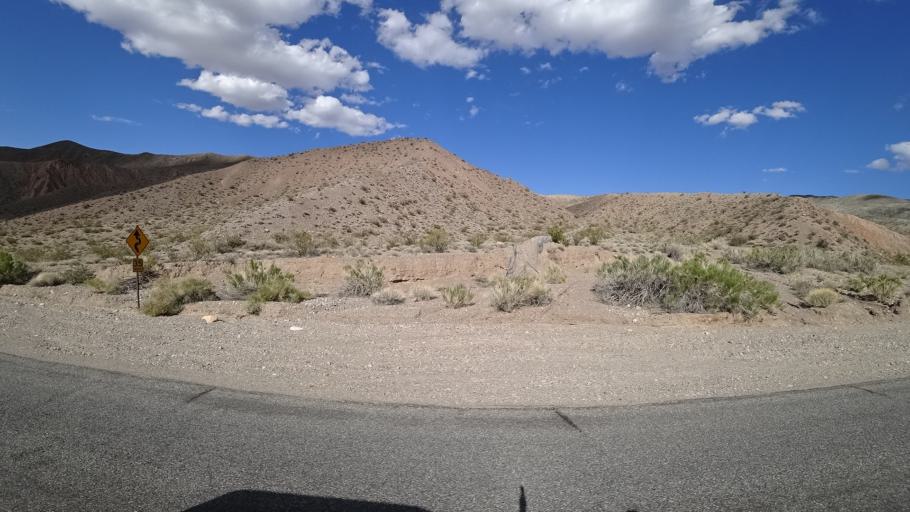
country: US
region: Nevada
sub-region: Nye County
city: Beatty
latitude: 36.4443
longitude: -117.1977
